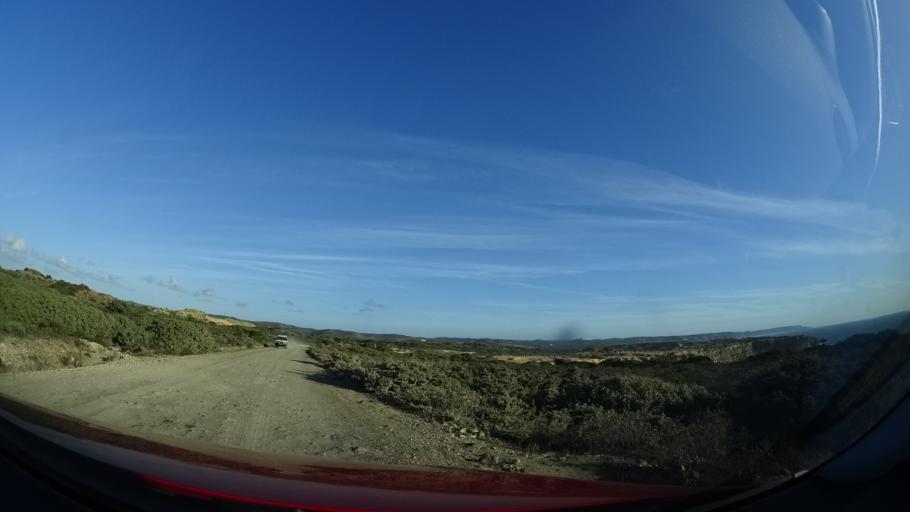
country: PT
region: Faro
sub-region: Vila do Bispo
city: Vila do Bispo
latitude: 37.1909
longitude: -8.9095
